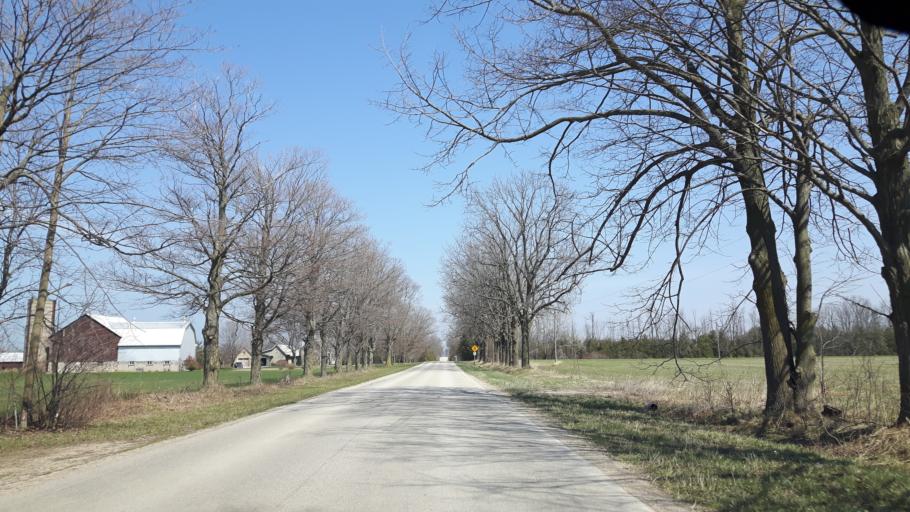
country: CA
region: Ontario
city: Goderich
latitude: 43.6538
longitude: -81.6846
